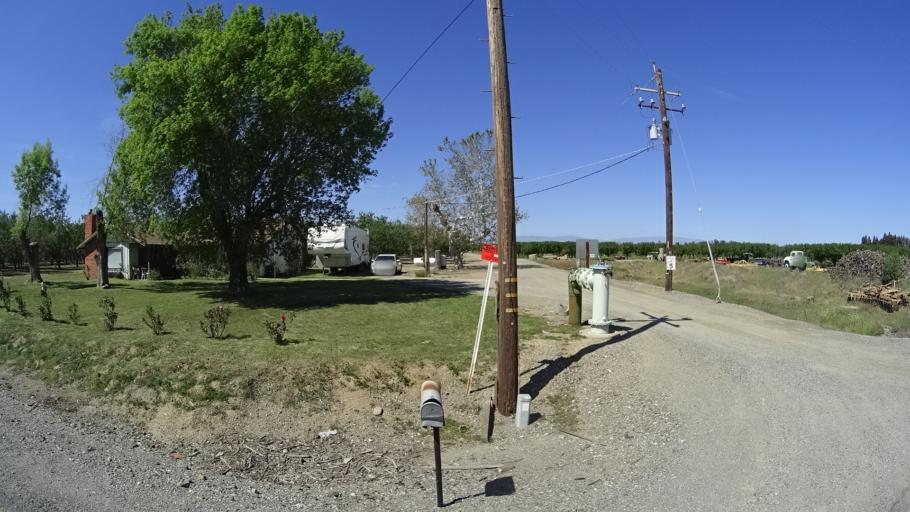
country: US
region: California
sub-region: Glenn County
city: Orland
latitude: 39.6743
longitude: -122.1405
